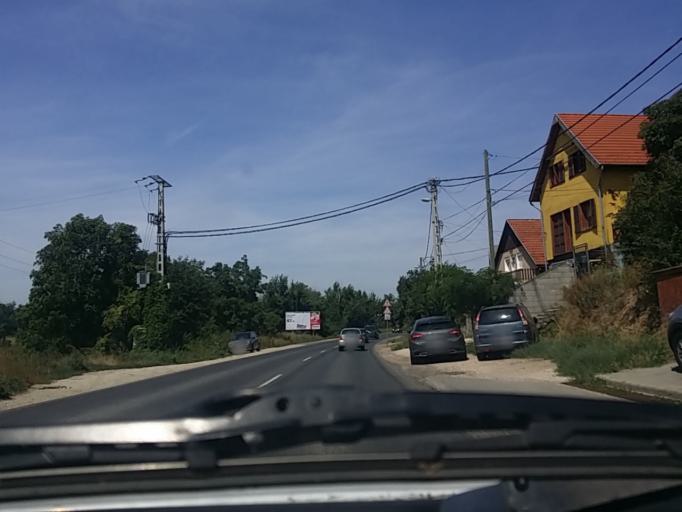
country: HU
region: Pest
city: Pilisborosjeno
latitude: 47.5888
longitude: 18.9893
